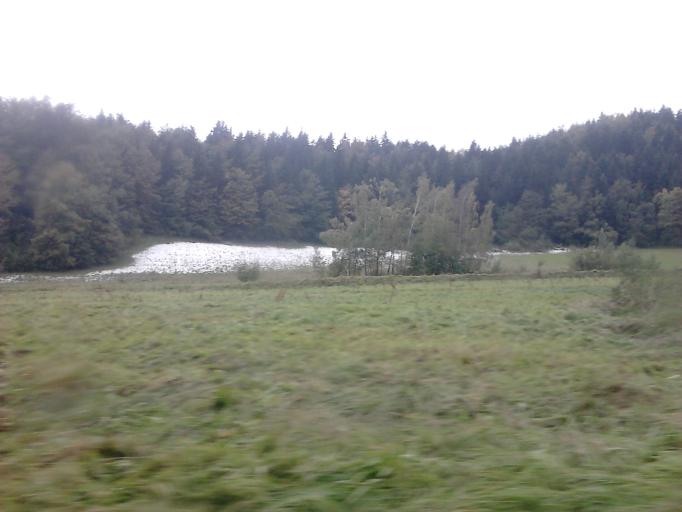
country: PL
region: Lesser Poland Voivodeship
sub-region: Powiat limanowski
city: Limanowa
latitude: 49.7174
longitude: 20.4652
